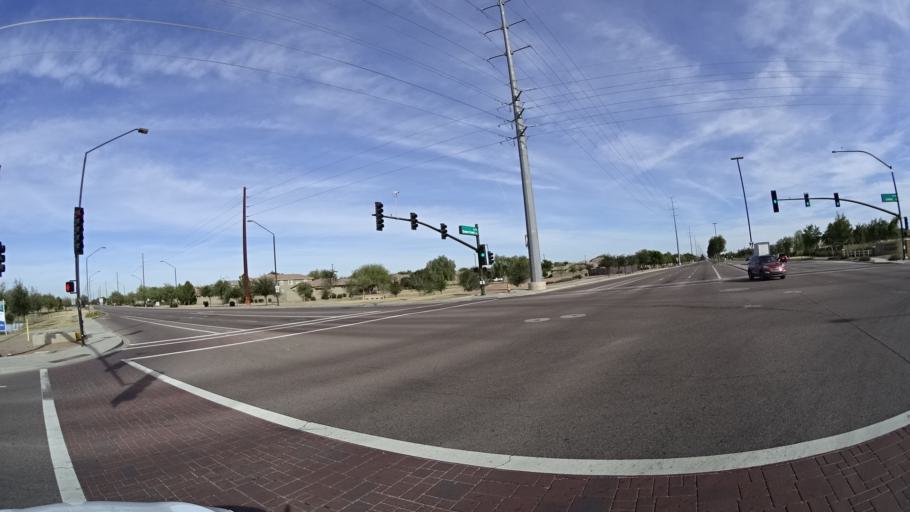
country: US
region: Arizona
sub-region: Maricopa County
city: Chandler
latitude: 33.2630
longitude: -111.7723
